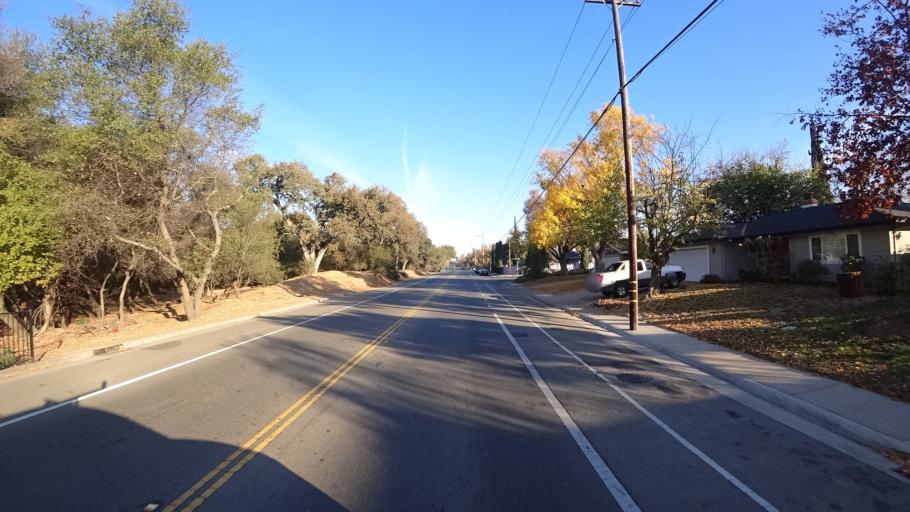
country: US
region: California
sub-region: Sacramento County
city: Antelope
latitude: 38.6960
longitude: -121.3087
